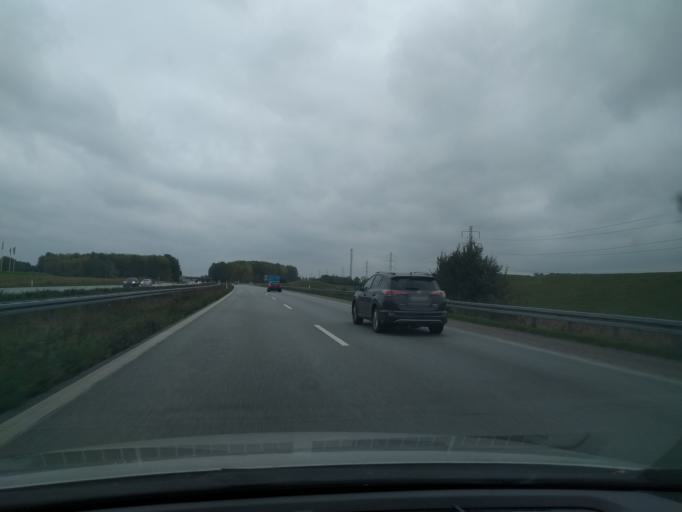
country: DK
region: Zealand
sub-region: Ringsted Kommune
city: Ringsted
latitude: 55.4561
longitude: 11.8131
